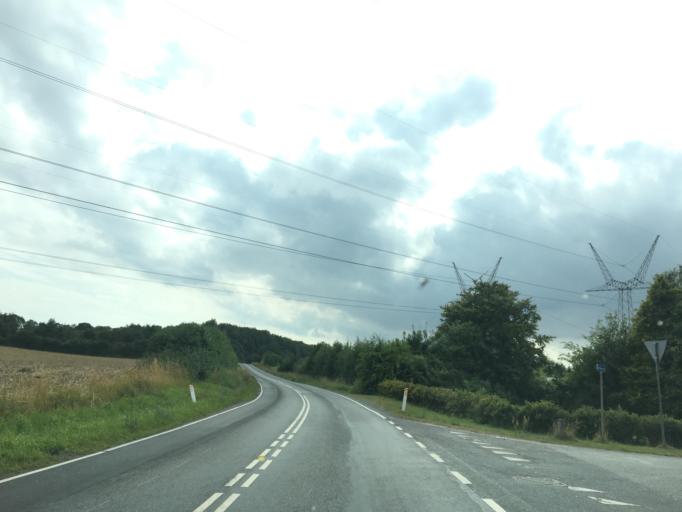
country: DK
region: South Denmark
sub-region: Assens Kommune
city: Arup
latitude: 55.4120
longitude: 10.0220
